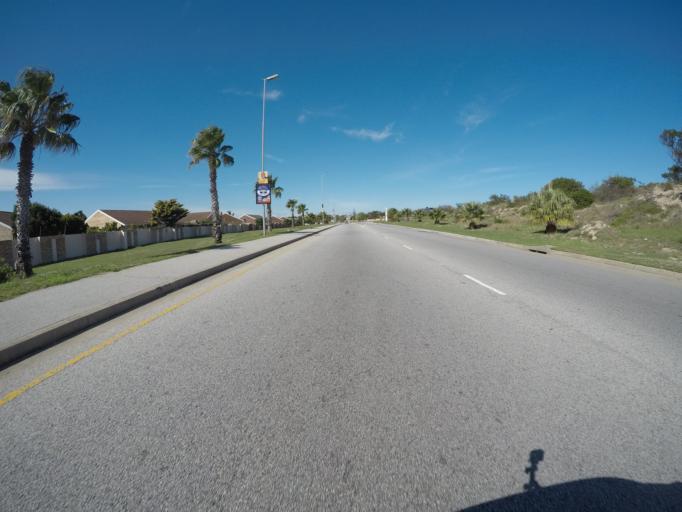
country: ZA
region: Eastern Cape
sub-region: Nelson Mandela Bay Metropolitan Municipality
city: Port Elizabeth
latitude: -33.9898
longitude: 25.6471
